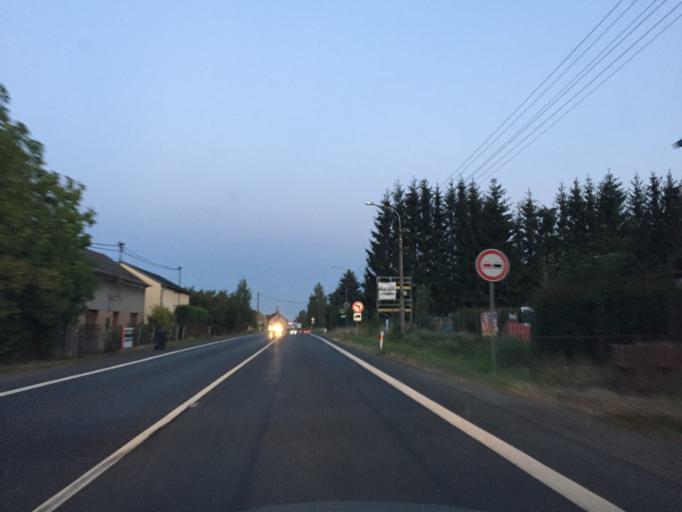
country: CZ
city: Cvikov
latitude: 50.7826
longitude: 14.6177
